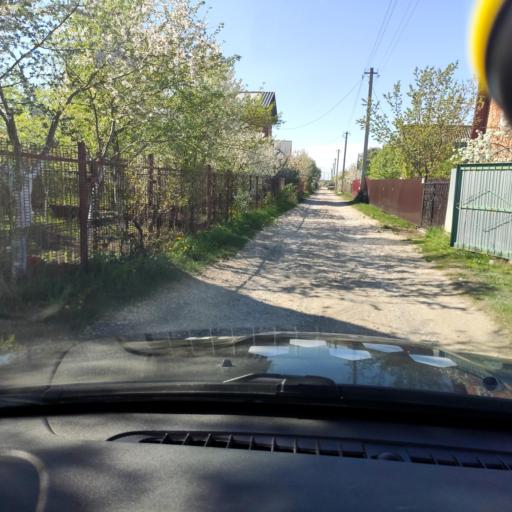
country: RU
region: Samara
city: Tol'yatti
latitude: 53.5946
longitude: 49.2896
